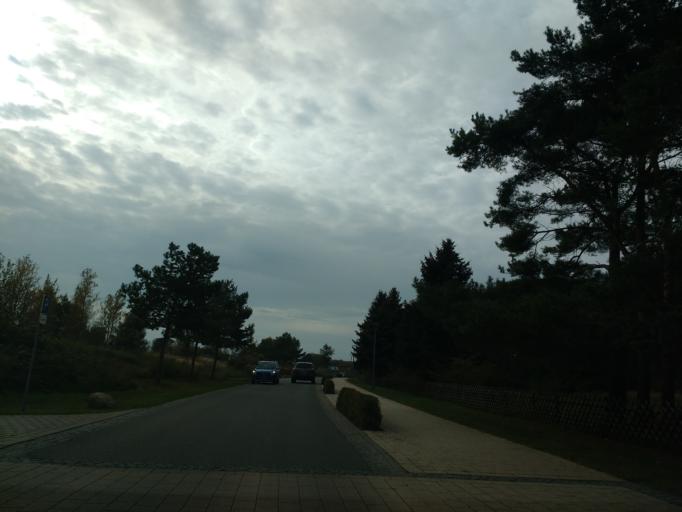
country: DE
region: Schleswig-Holstein
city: Gromitz
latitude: 54.1580
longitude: 10.9950
